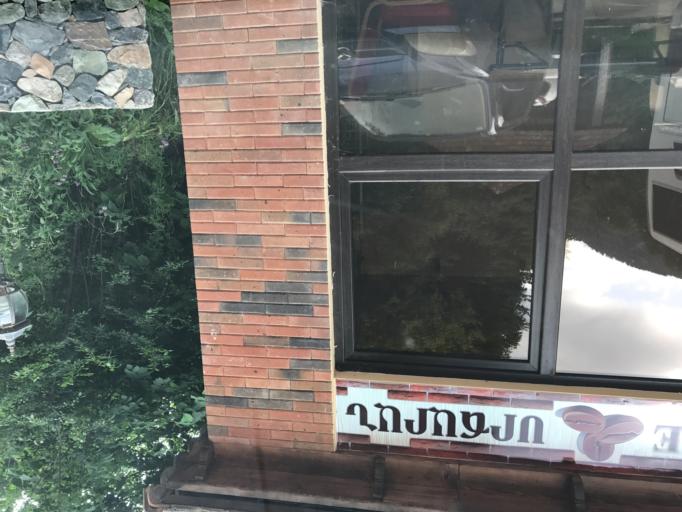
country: AM
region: Tavush
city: Dilijan
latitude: 40.8063
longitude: 44.8924
